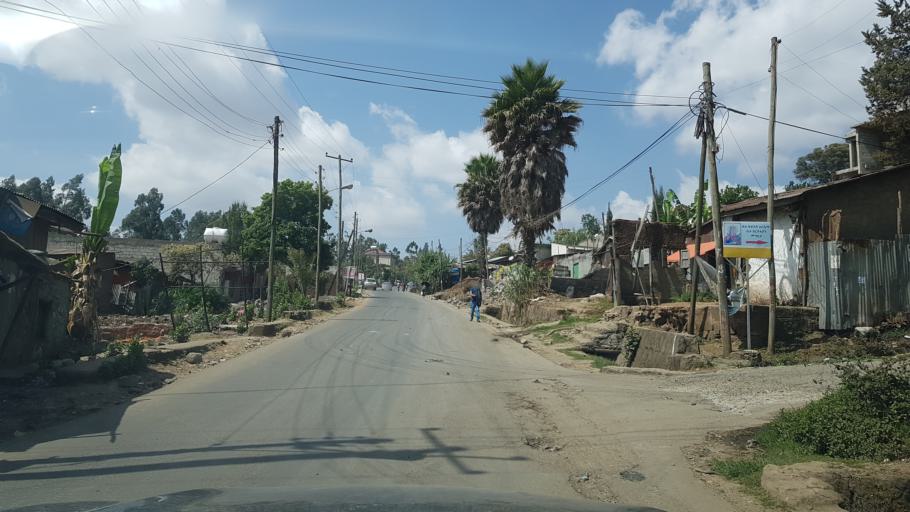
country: ET
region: Adis Abeba
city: Addis Ababa
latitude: 9.0072
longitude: 38.7102
